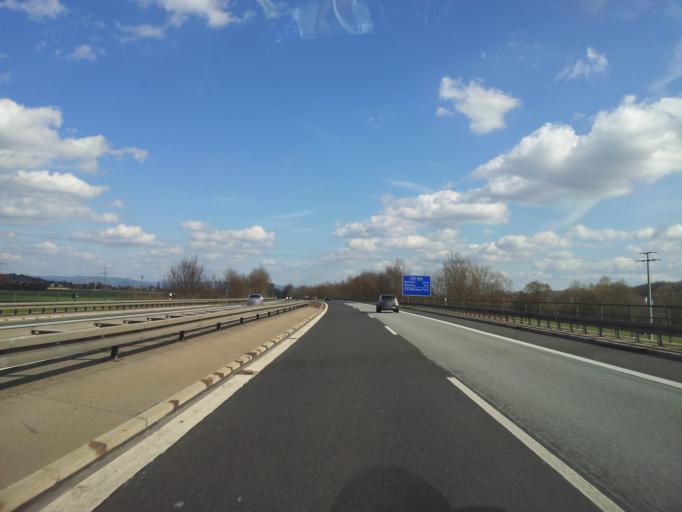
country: DE
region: Bavaria
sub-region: Upper Franconia
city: Viereth-Trunstadt
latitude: 49.9289
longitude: 10.7871
